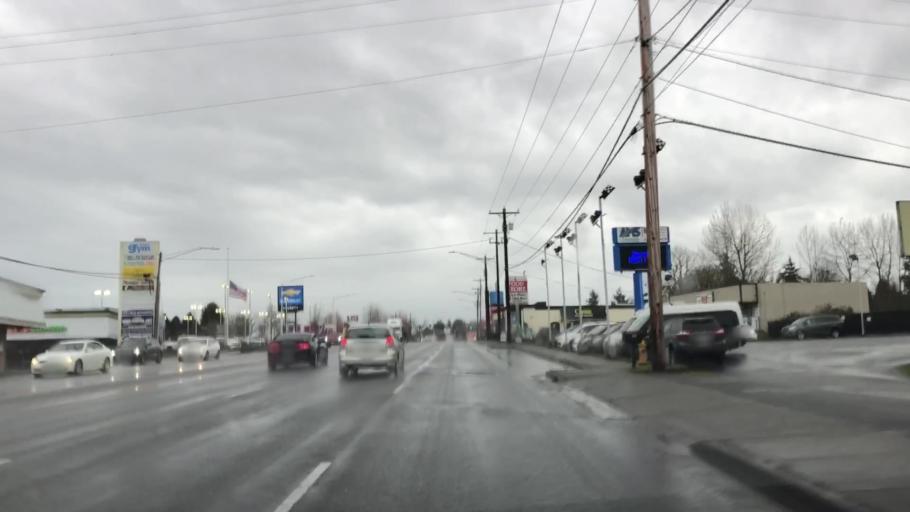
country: US
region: Washington
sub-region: Snohomish County
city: Everett
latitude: 47.9330
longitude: -122.2200
